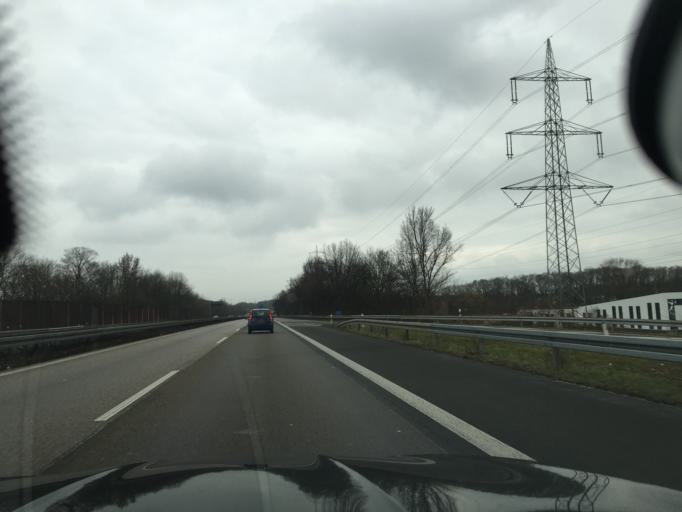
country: DE
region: North Rhine-Westphalia
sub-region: Regierungsbezirk Koln
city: Wahn-Heide
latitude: 50.8575
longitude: 7.0969
